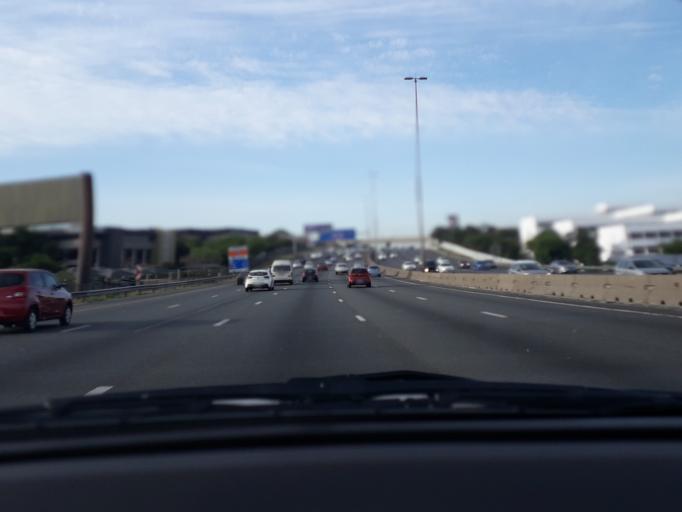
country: ZA
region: Gauteng
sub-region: City of Johannesburg Metropolitan Municipality
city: Midrand
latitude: -26.0039
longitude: 28.1208
